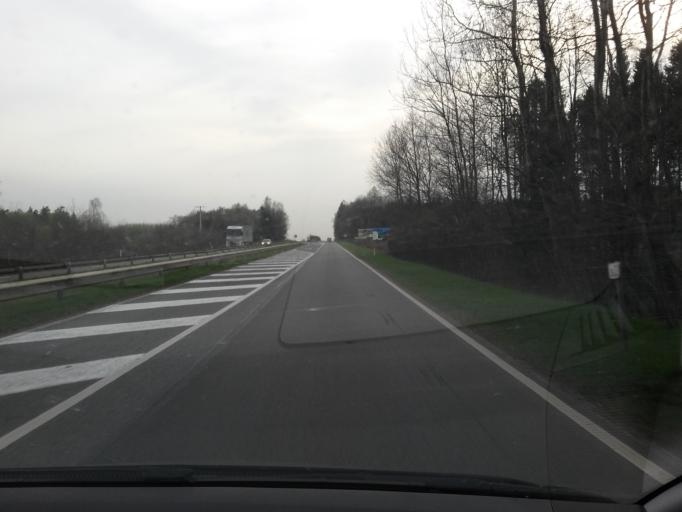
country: BE
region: Wallonia
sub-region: Province du Luxembourg
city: Bertrix
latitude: 49.8843
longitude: 5.2777
